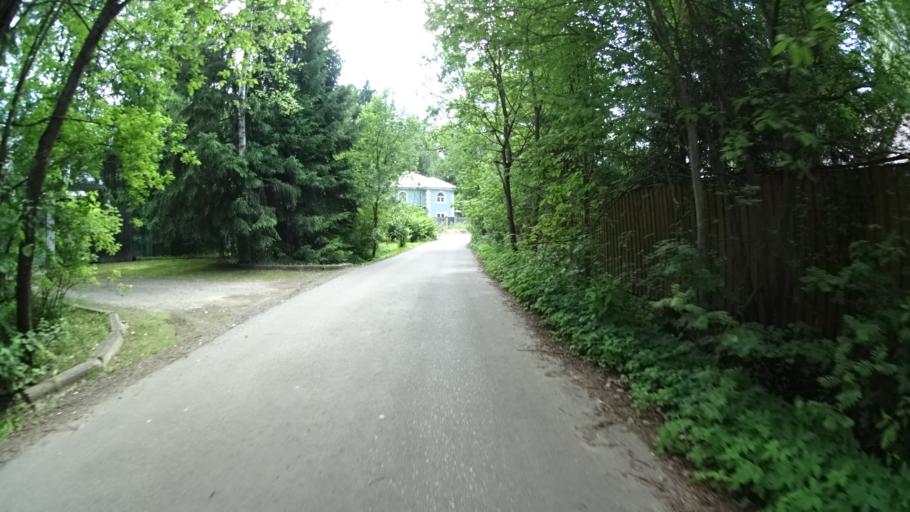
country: RU
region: Moskovskaya
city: Zelenogradskiy
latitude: 56.0981
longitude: 37.8985
